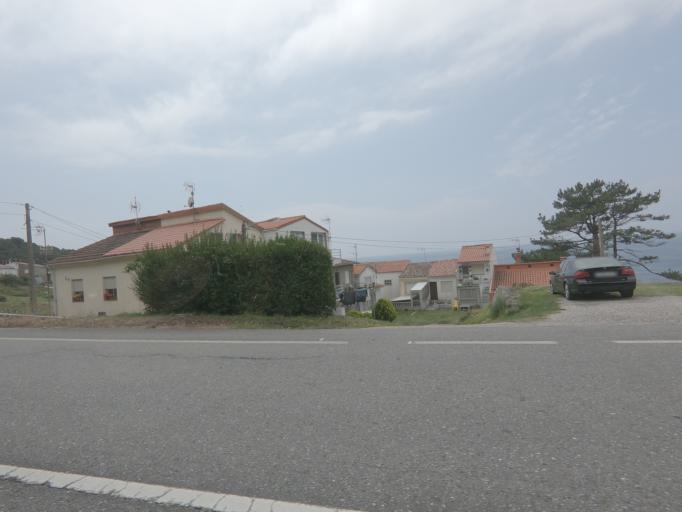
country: ES
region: Galicia
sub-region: Provincia de Pontevedra
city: Oia
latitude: 41.9537
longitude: -8.8826
